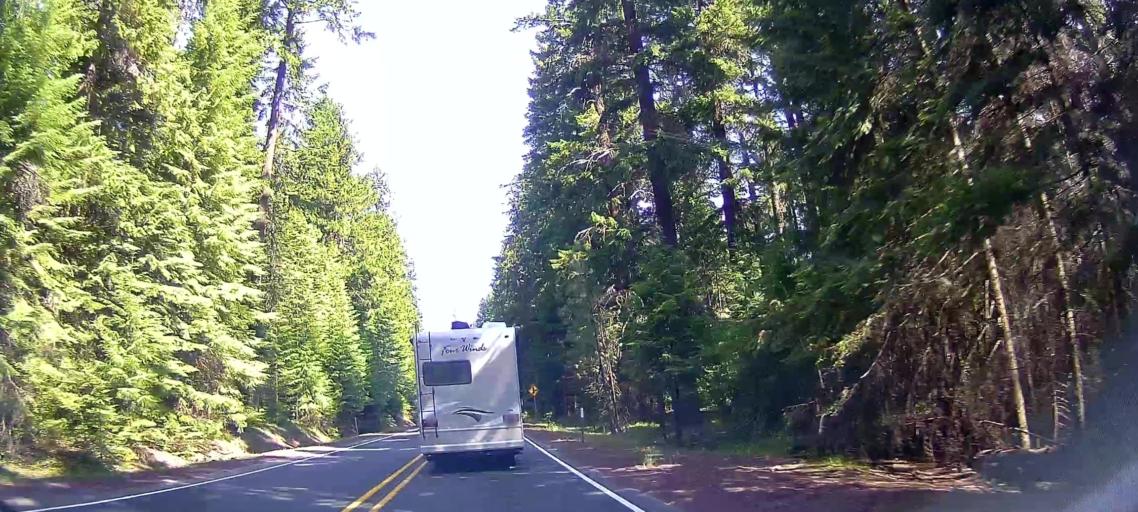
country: US
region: Oregon
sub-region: Jefferson County
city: Warm Springs
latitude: 45.0851
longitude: -121.5440
